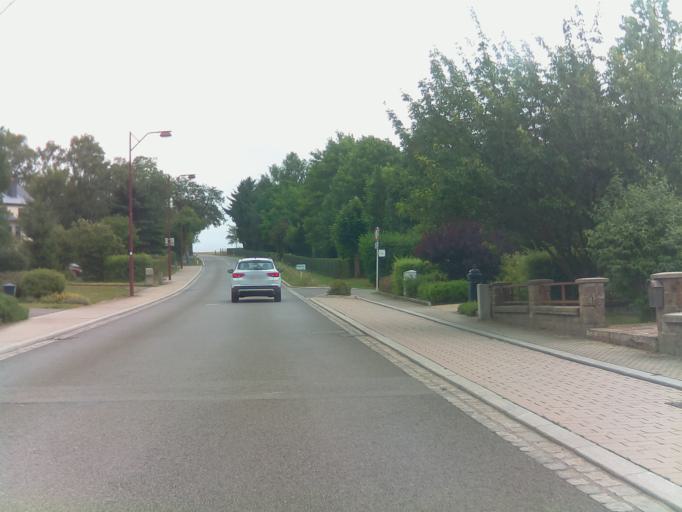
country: LU
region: Luxembourg
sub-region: Canton de Capellen
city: Koerich
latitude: 49.6498
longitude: 5.9395
